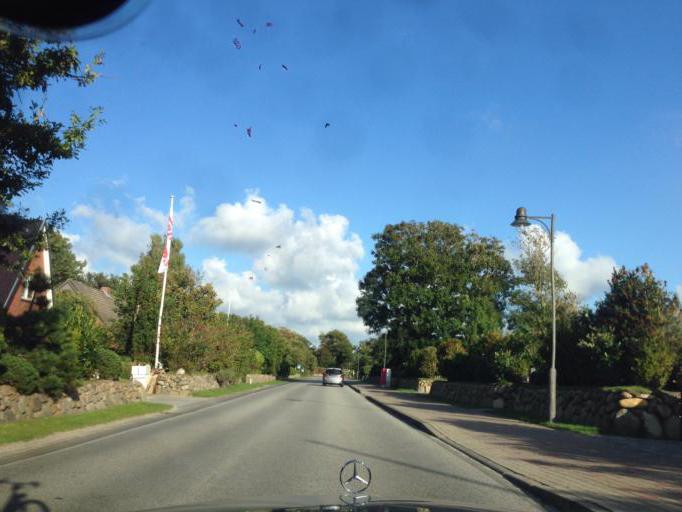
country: DE
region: Schleswig-Holstein
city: Sylt-Ost
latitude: 54.8731
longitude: 8.3966
